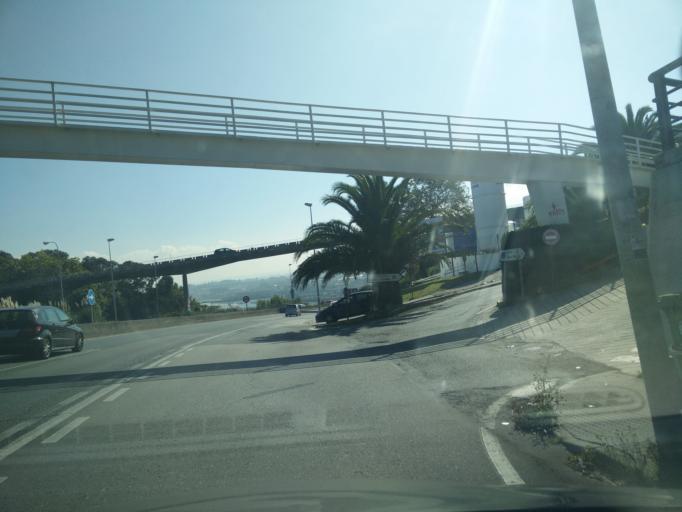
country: ES
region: Galicia
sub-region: Provincia da Coruna
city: A Coruna
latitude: 43.3450
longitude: -8.3870
